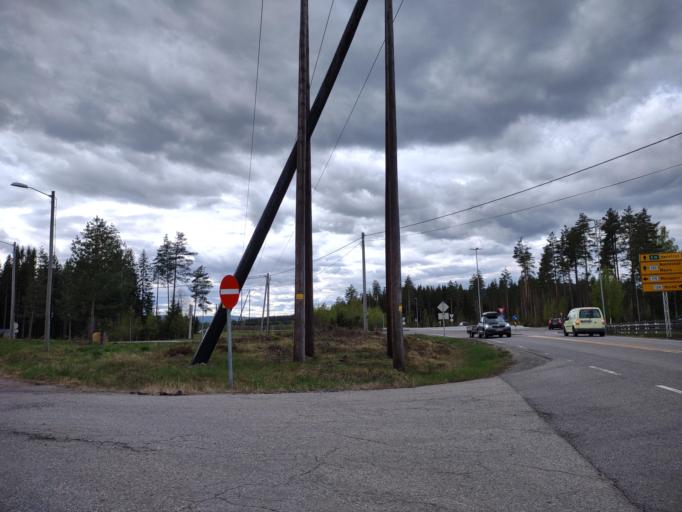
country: NO
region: Akershus
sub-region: Nannestad
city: Maura
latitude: 60.2537
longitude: 11.1009
